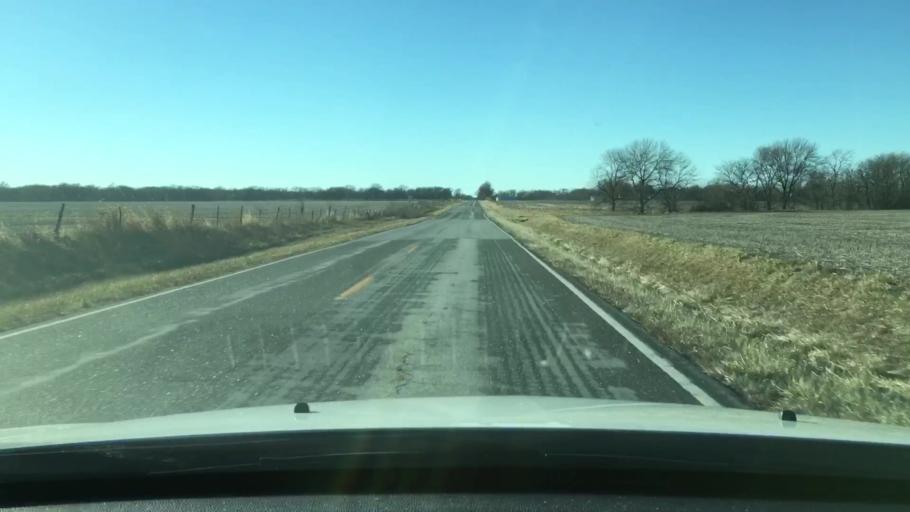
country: US
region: Missouri
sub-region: Audrain County
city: Mexico
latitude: 39.2815
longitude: -91.7033
